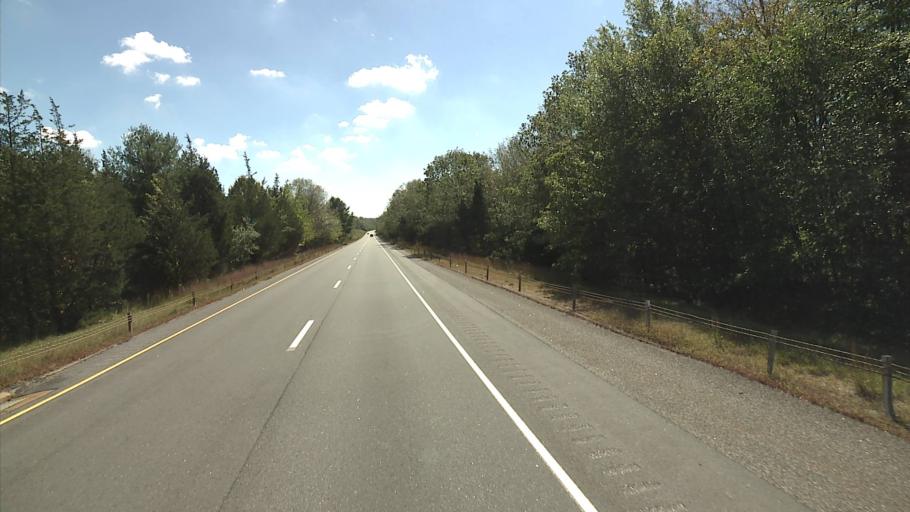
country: US
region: Connecticut
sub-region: New London County
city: Colchester
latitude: 41.5311
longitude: -72.3093
